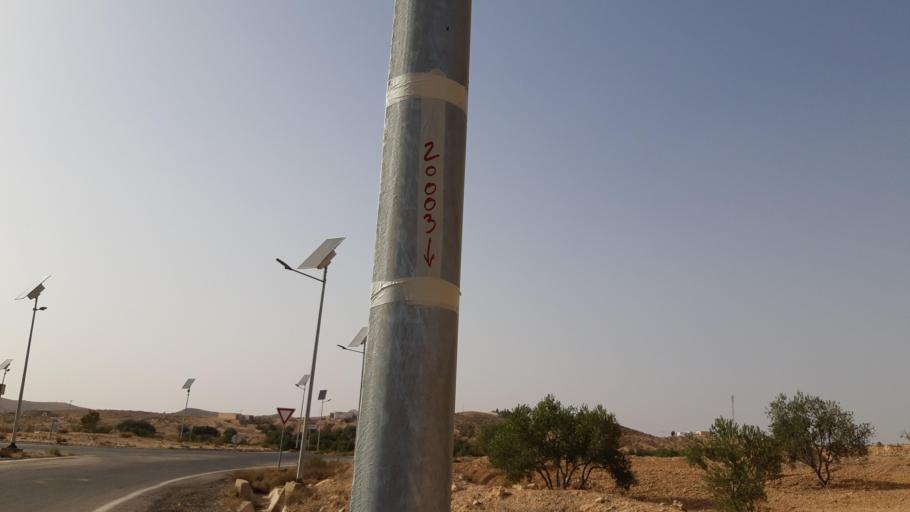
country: TN
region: Qabis
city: Matmata
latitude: 33.5044
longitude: 10.0096
